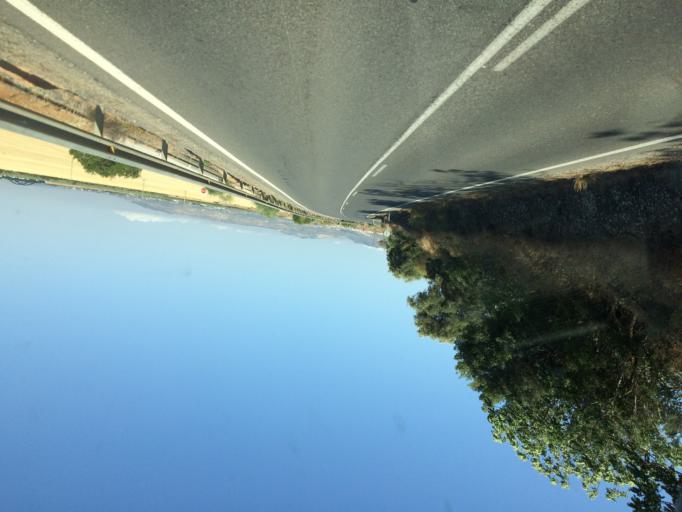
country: ES
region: Andalusia
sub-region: Provincia de Malaga
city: Antequera
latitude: 37.0541
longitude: -4.4980
